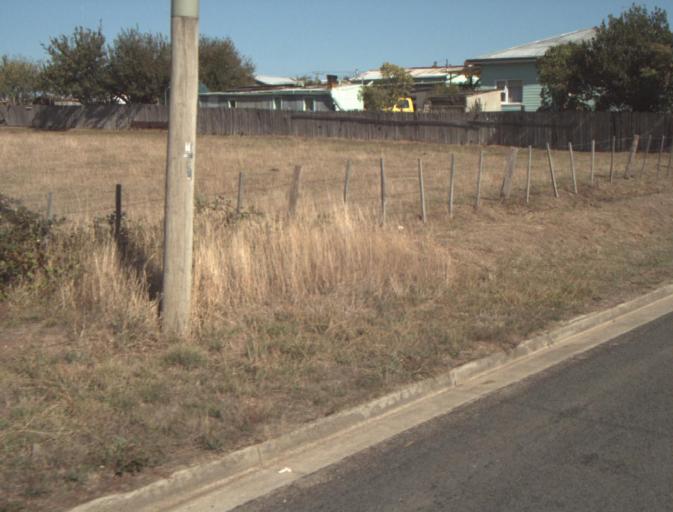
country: AU
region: Tasmania
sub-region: Launceston
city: Mayfield
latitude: -41.3691
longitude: 147.1404
